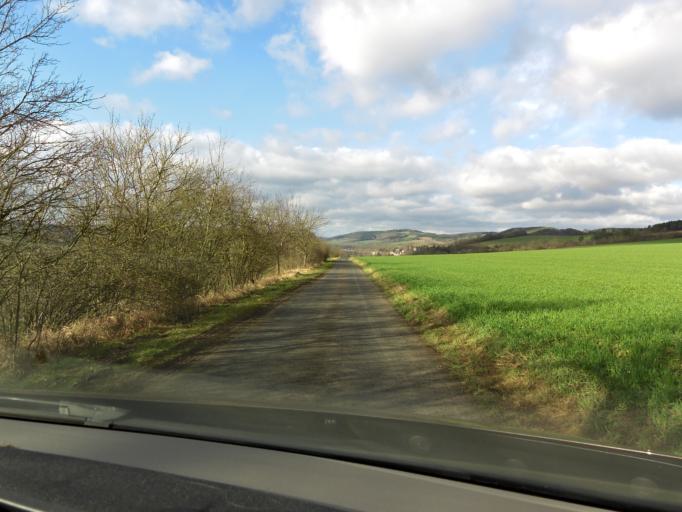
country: DE
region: Thuringia
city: Krauthausen
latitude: 51.0406
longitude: 10.2696
